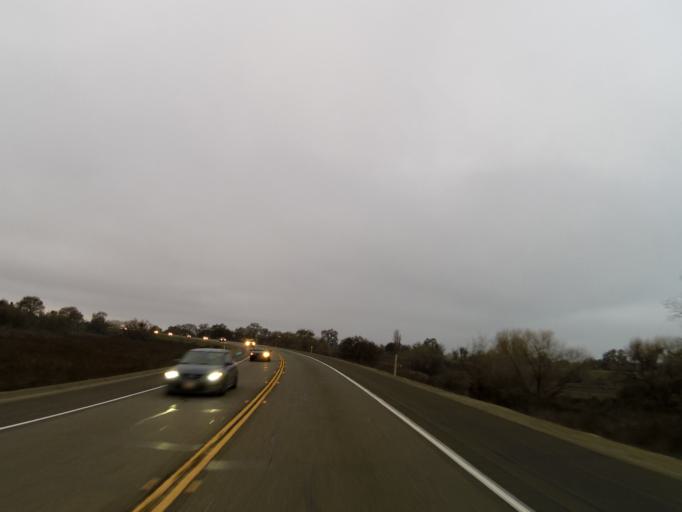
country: US
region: California
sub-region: San Joaquin County
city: Ripon
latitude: 37.6414
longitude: -121.2199
